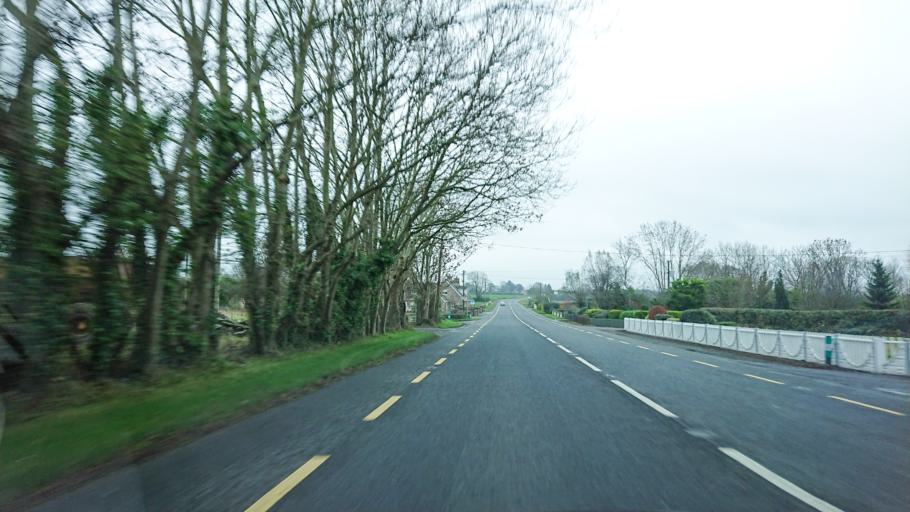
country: IE
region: Leinster
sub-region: Kilkenny
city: Mooncoin
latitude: 52.2858
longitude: -7.2161
